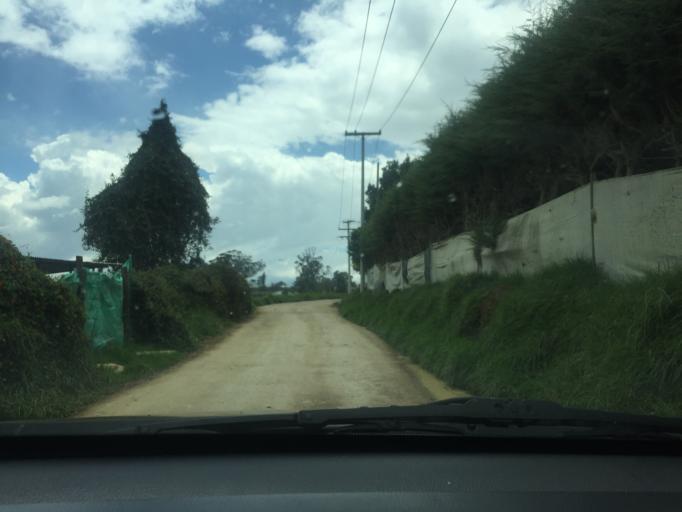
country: CO
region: Cundinamarca
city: Facatativa
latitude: 4.8011
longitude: -74.3043
